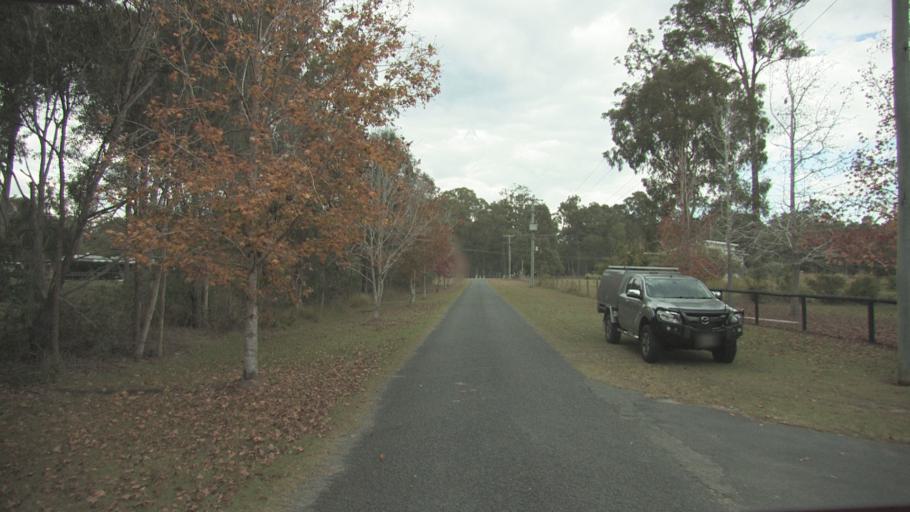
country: AU
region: Queensland
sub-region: Logan
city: Chambers Flat
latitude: -27.7823
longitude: 153.1126
